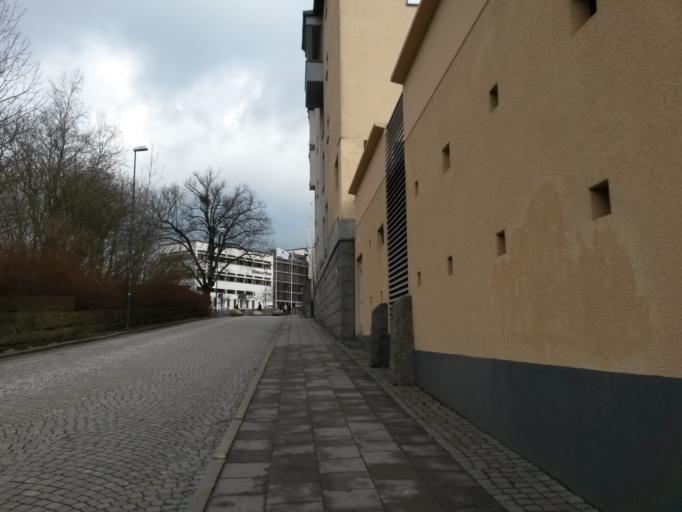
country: SE
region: Vaestra Goetaland
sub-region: Boras Kommun
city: Boras
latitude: 57.7242
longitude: 12.9381
